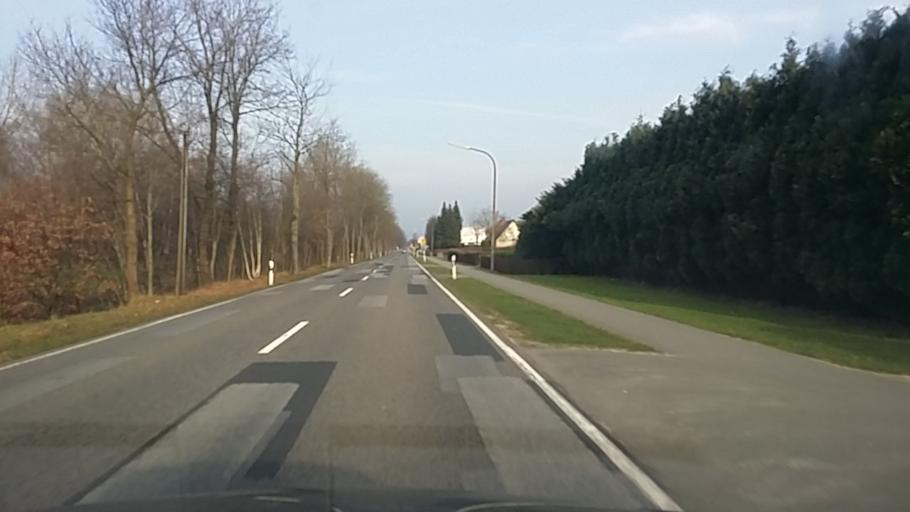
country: DE
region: Lower Saxony
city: Twist
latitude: 52.6307
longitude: 7.0982
